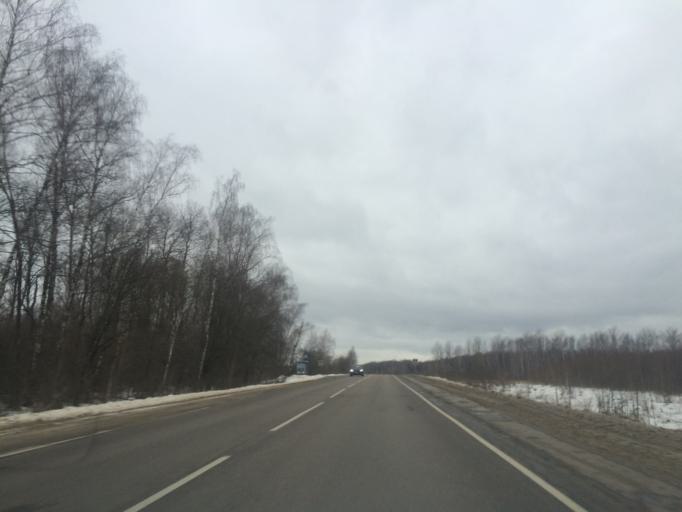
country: RU
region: Tula
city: Pervomayskiy
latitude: 54.1328
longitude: 37.3556
